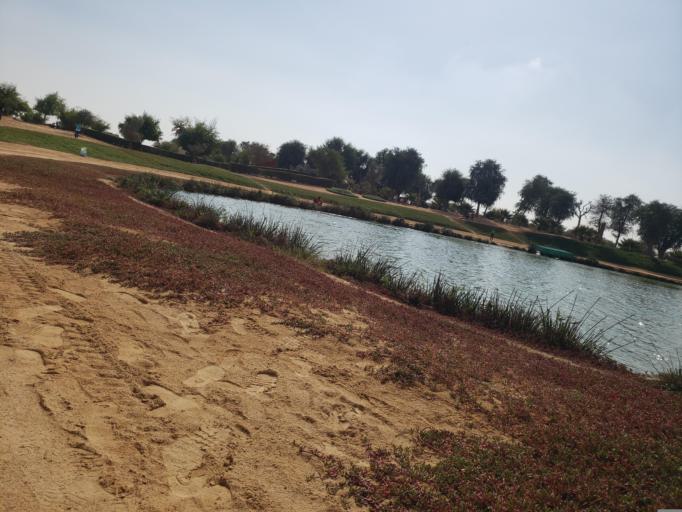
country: AE
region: Dubai
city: Dubai
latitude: 24.8544
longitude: 55.2503
